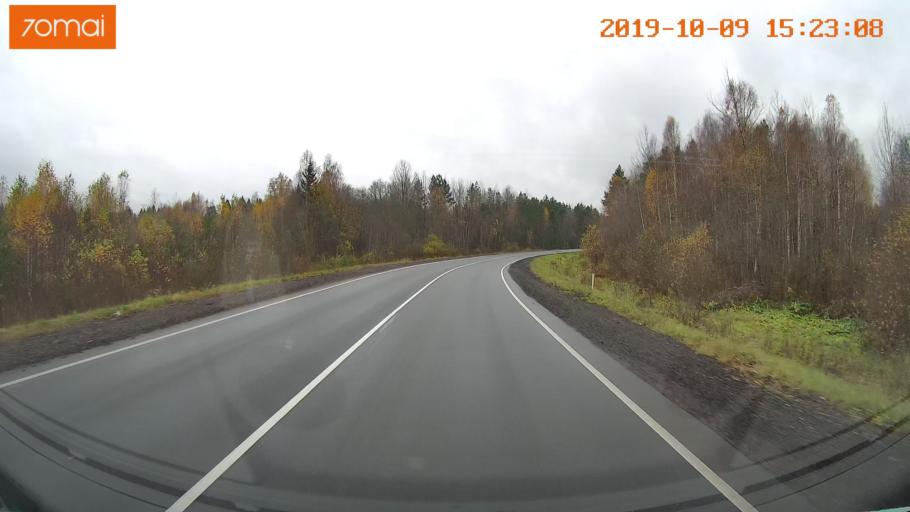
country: RU
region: Kostroma
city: Susanino
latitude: 58.0376
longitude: 41.4864
